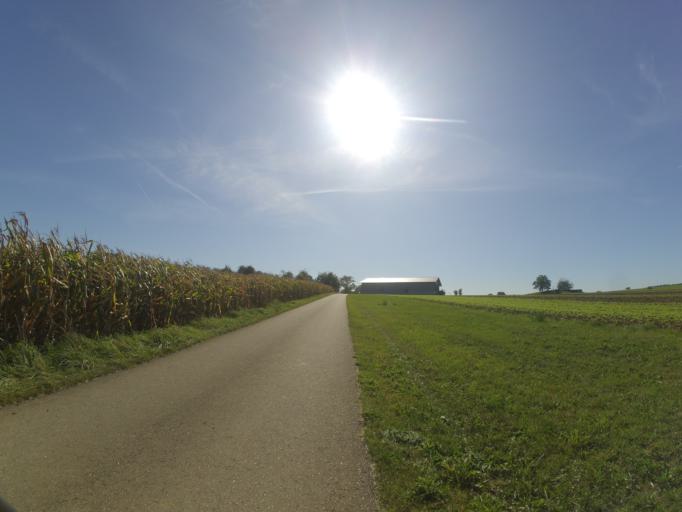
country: DE
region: Baden-Wuerttemberg
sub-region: Tuebingen Region
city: Nerenstetten
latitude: 48.5312
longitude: 10.0949
